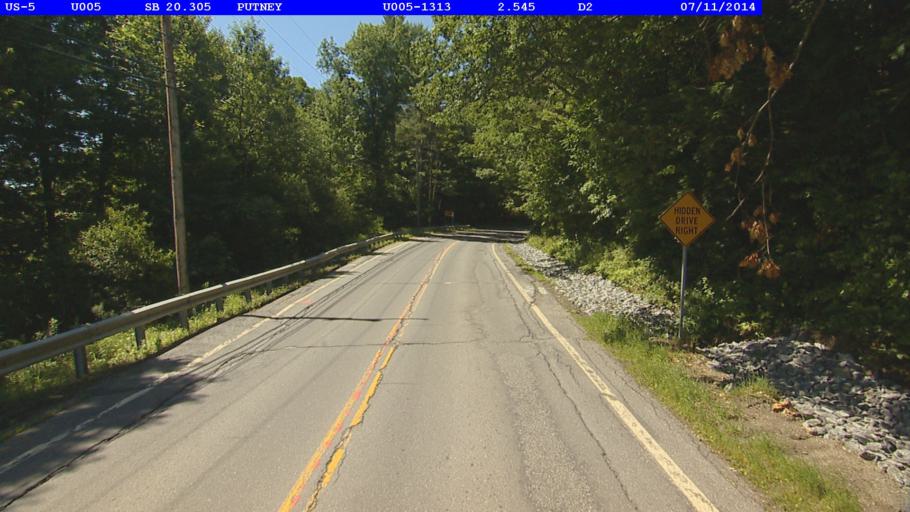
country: US
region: New Hampshire
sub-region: Cheshire County
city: Westmoreland
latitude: 42.9939
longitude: -72.4969
